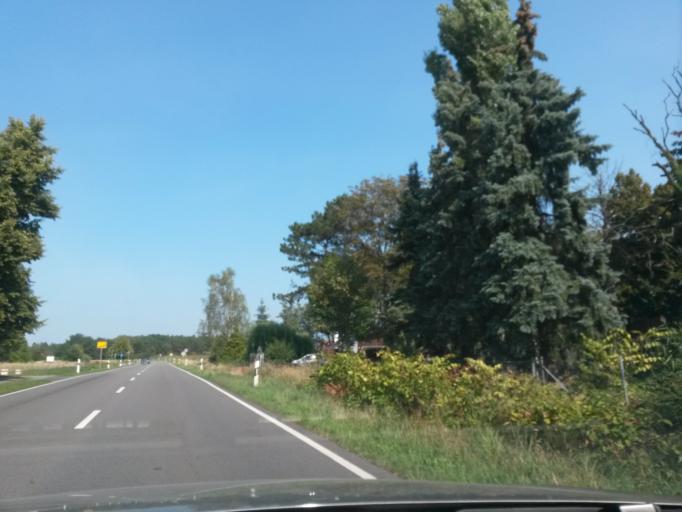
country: DE
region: Saxony-Anhalt
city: Tangermunde
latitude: 52.5431
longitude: 12.0179
